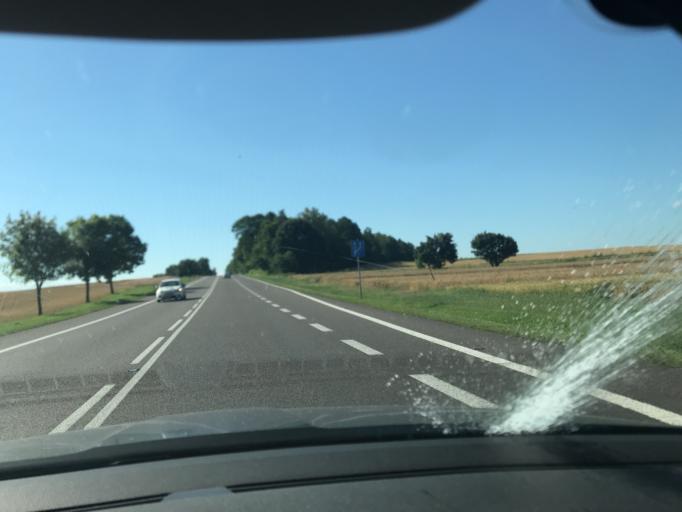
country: PL
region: Lublin Voivodeship
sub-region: Powiat krasnostawski
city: Izbica
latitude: 50.8681
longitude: 23.1512
